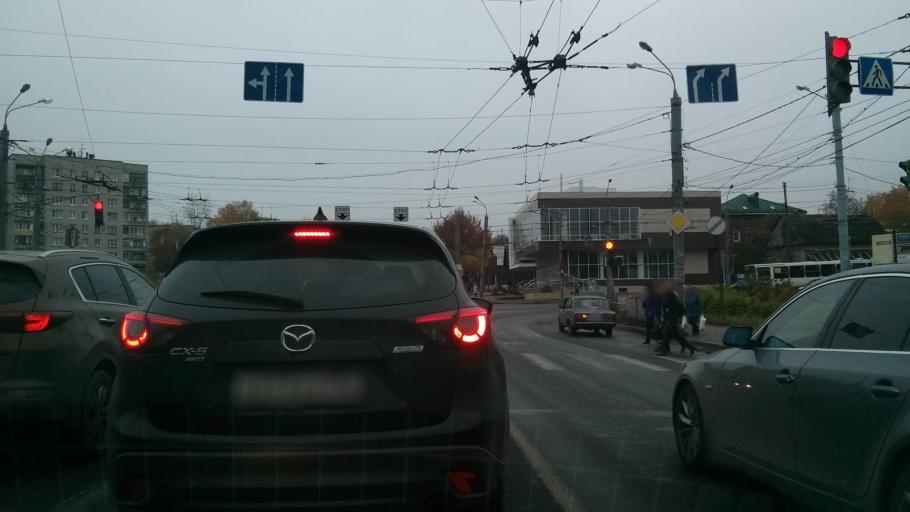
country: RU
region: Nizjnij Novgorod
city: Nizhniy Novgorod
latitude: 56.2967
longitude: 44.0339
